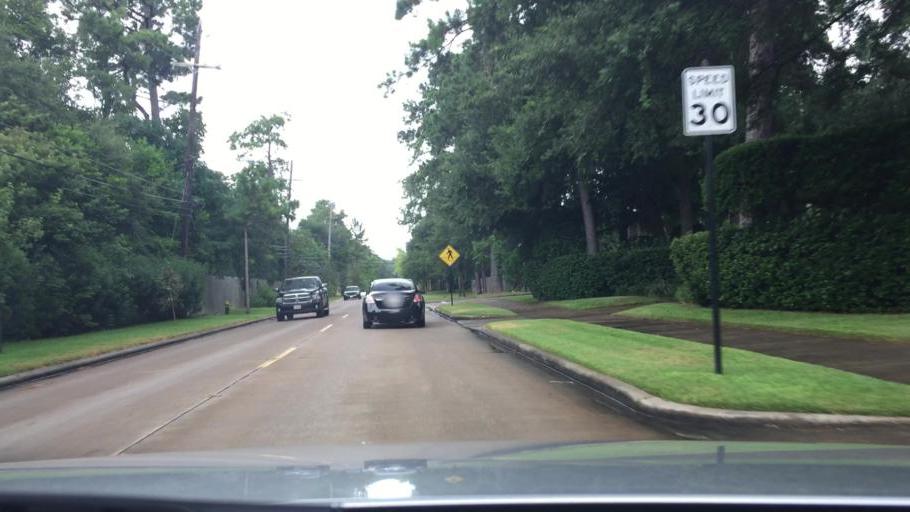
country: US
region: Texas
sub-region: Harris County
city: Hedwig Village
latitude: 29.7785
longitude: -95.5213
